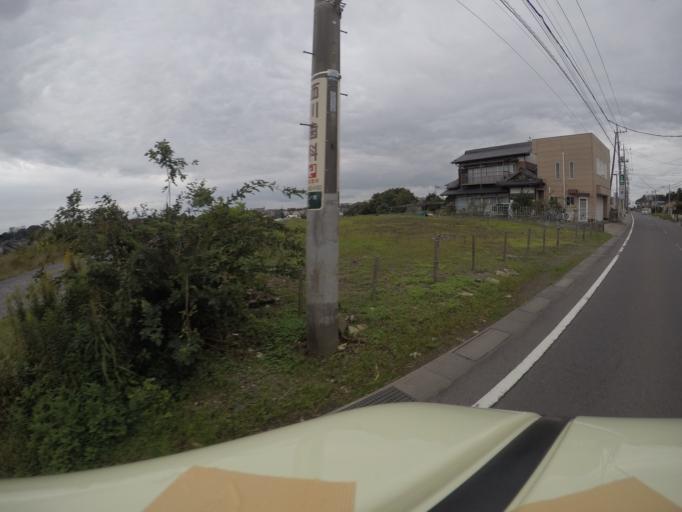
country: JP
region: Ibaraki
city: Naka
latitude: 36.0798
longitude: 140.1342
